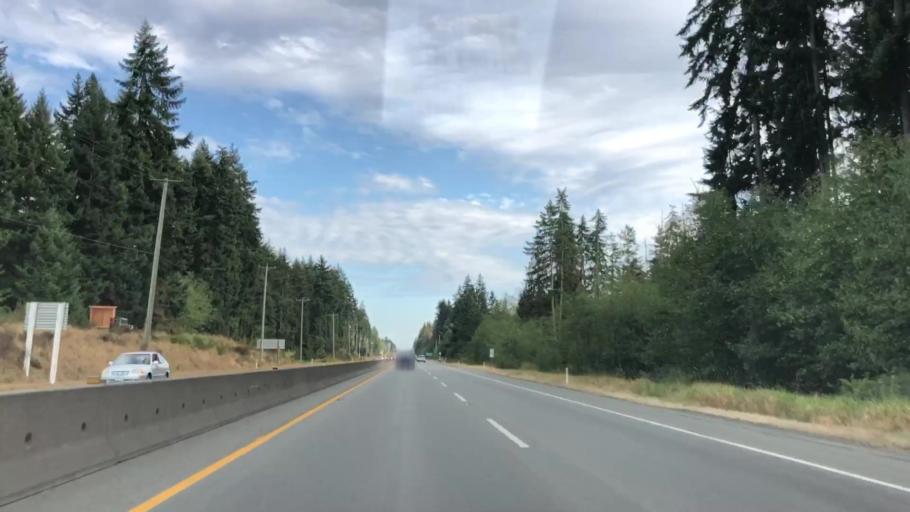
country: CA
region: British Columbia
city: Duncan
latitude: 48.7049
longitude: -123.6040
